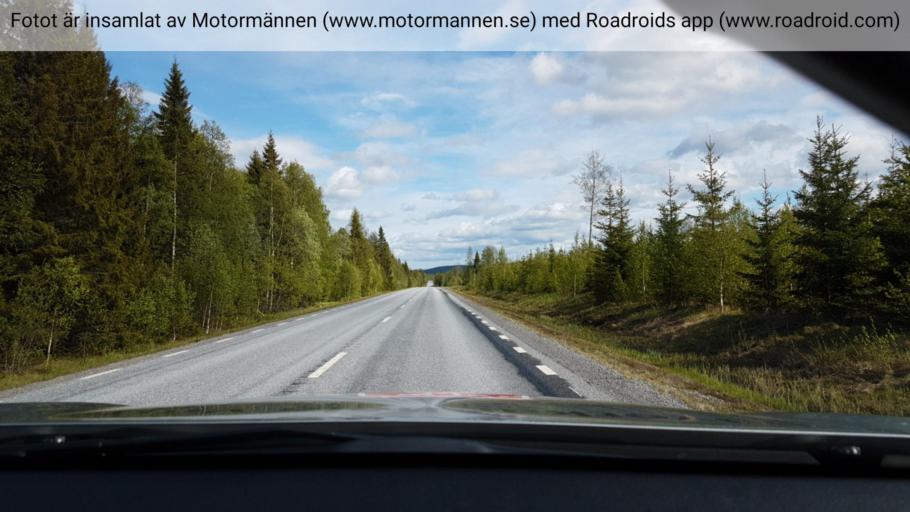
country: SE
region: Vaesterbotten
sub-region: Bjurholms Kommun
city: Bjurholm
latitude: 63.9484
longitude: 18.9023
